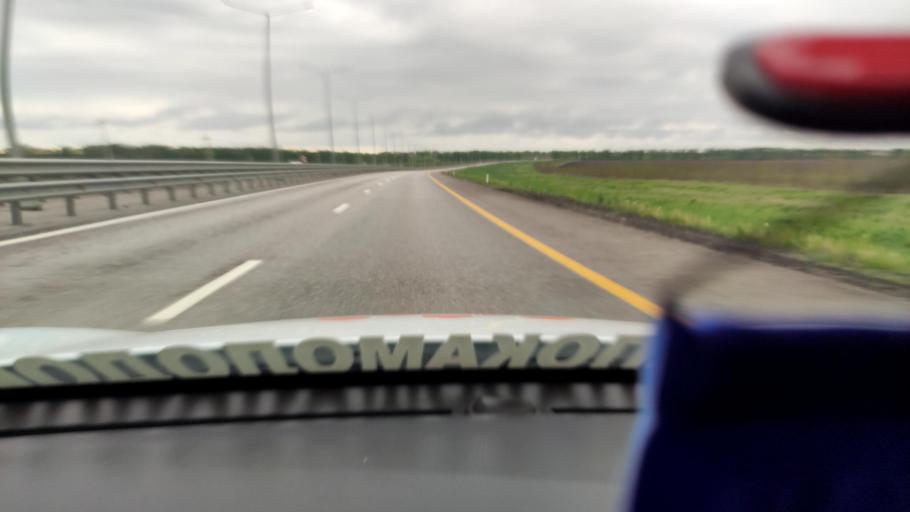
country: RU
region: Voronezj
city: Podkletnoye
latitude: 51.5848
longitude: 39.4506
